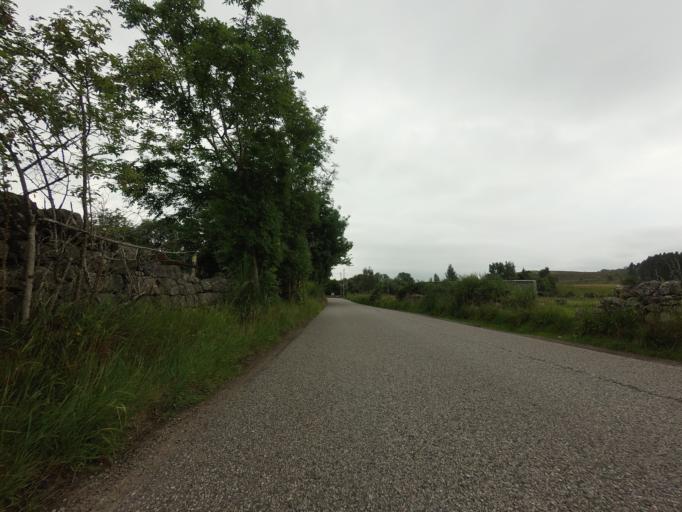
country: GB
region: Scotland
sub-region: Highland
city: Evanton
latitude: 57.8858
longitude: -4.3806
